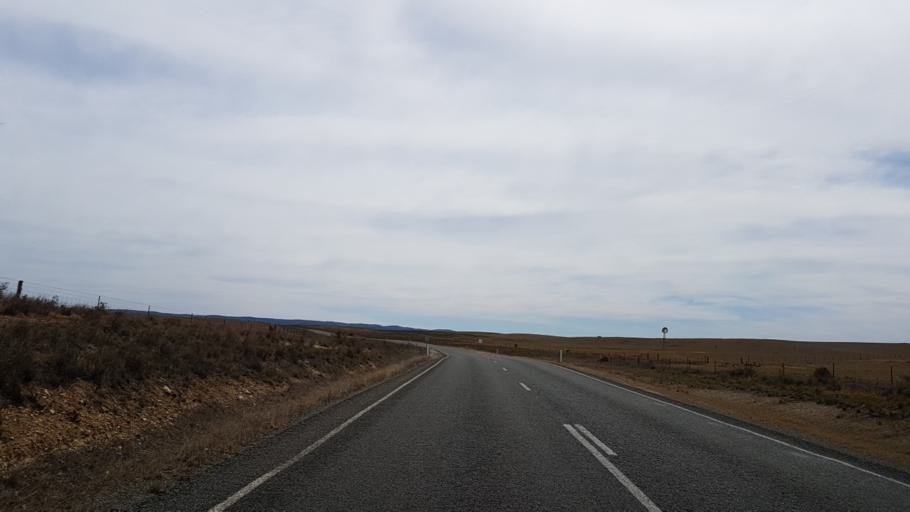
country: AU
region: South Australia
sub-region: Peterborough
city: Peterborough
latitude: -33.0237
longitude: 138.7214
